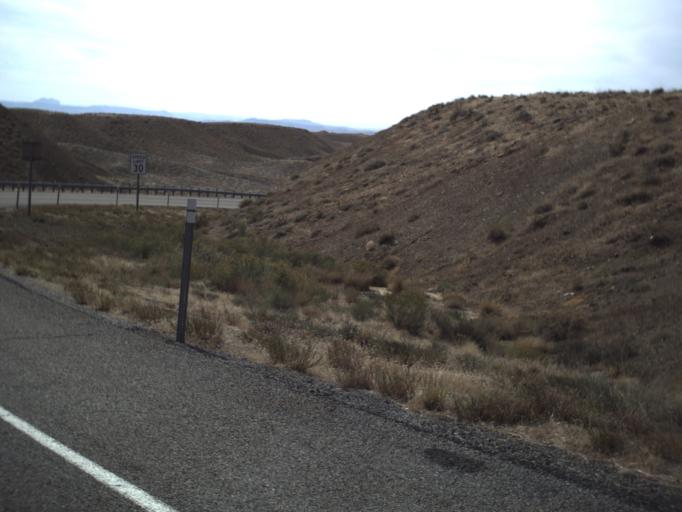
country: US
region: Utah
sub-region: Grand County
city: Moab
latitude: 38.9378
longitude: -109.8287
